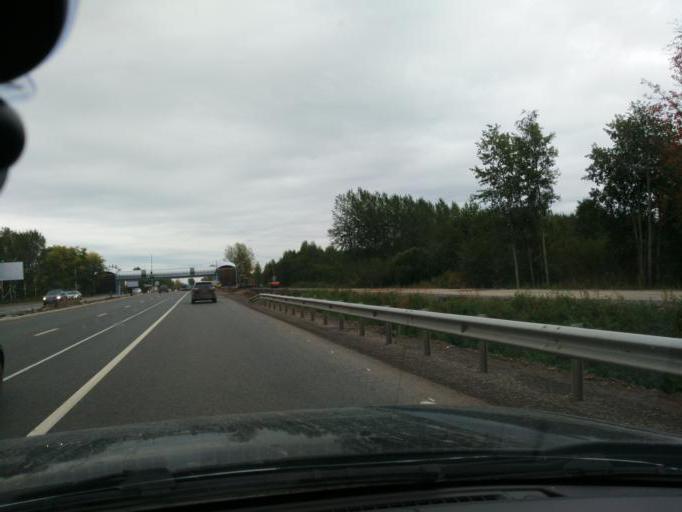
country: RU
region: Perm
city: Kondratovo
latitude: 57.9412
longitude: 56.0599
